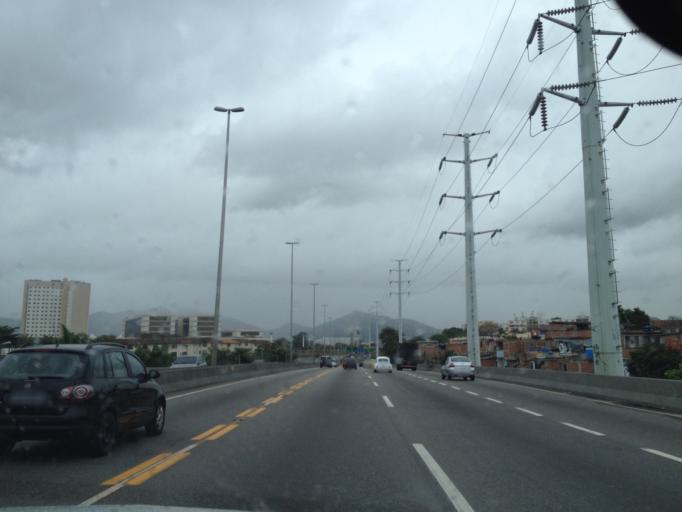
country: BR
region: Rio de Janeiro
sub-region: Rio De Janeiro
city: Rio de Janeiro
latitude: -22.8724
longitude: -43.2667
